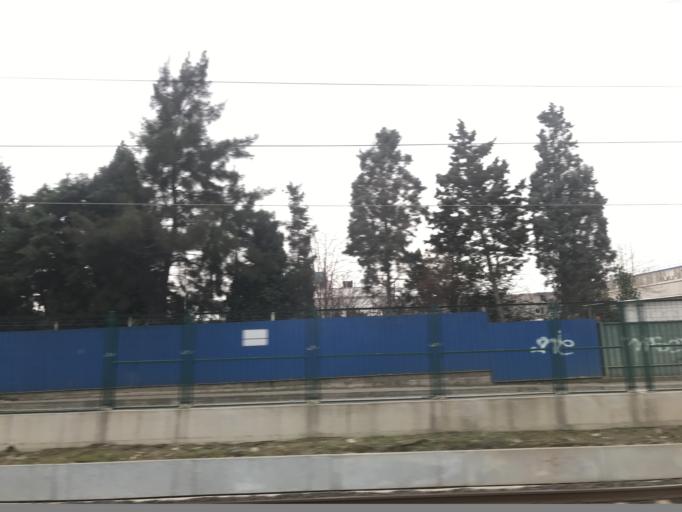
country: TR
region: Kocaeli
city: Darica
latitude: 40.7975
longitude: 29.3825
